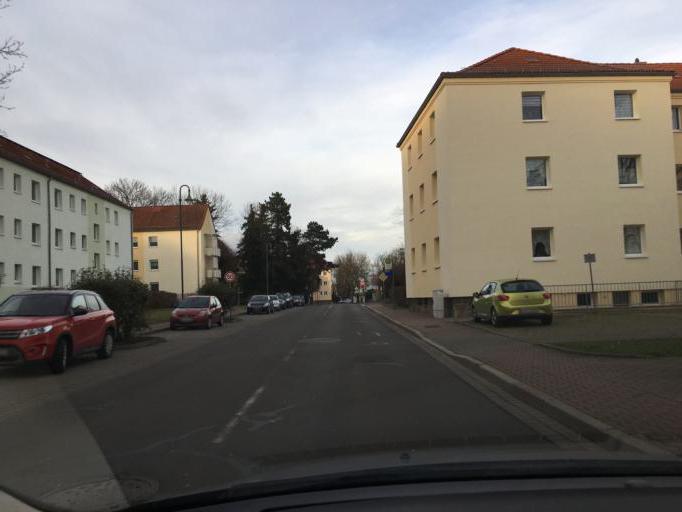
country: DE
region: Saxony
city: Grossposna
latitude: 51.2856
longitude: 12.4657
